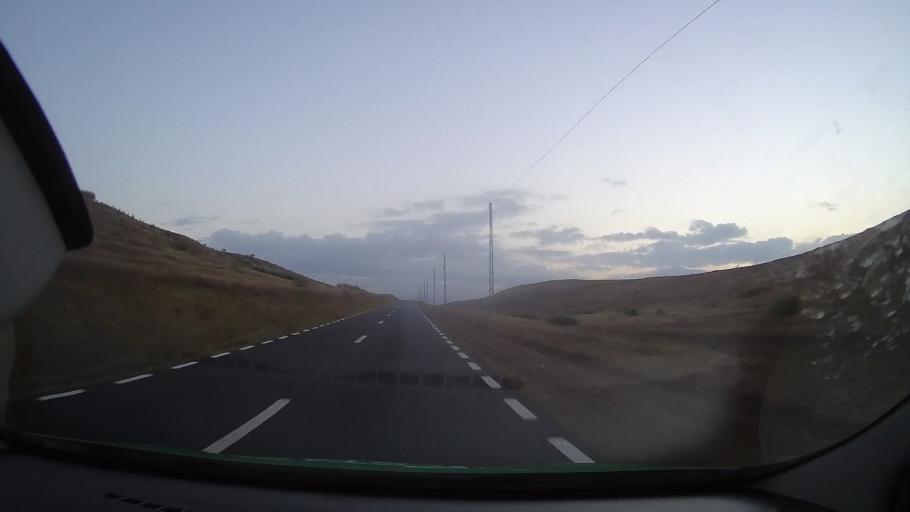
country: RO
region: Constanta
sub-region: Comuna Oltina
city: Oltina
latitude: 44.1477
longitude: 27.6669
